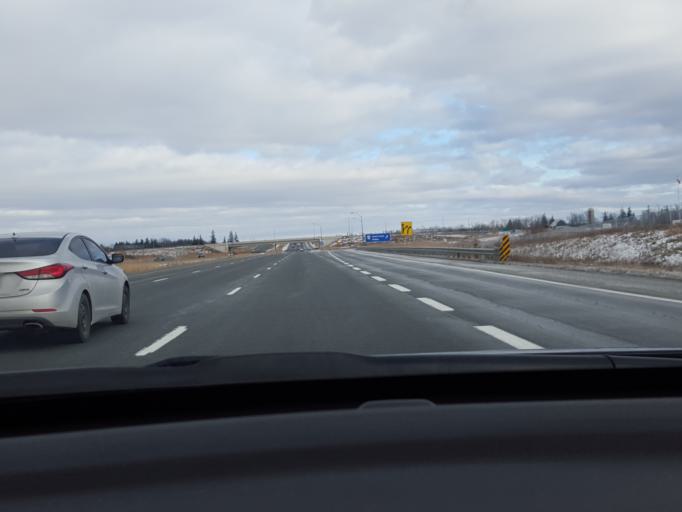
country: CA
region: Ontario
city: Markham
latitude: 43.8728
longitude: -79.2214
